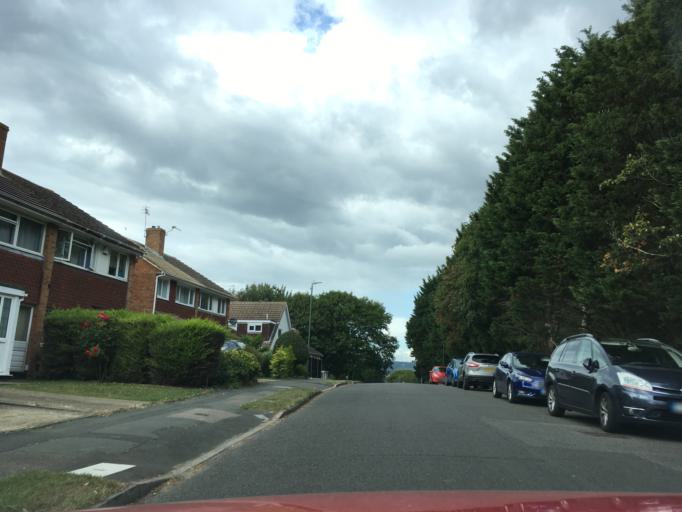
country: GB
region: England
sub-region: Kent
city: Maidstone
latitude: 51.2597
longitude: 0.5230
